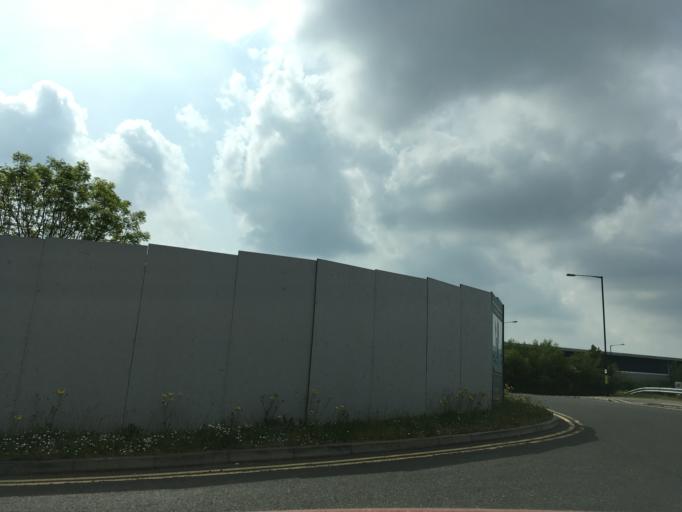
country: GB
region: England
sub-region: South Gloucestershire
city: Severn Beach
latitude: 51.5180
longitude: -2.6669
